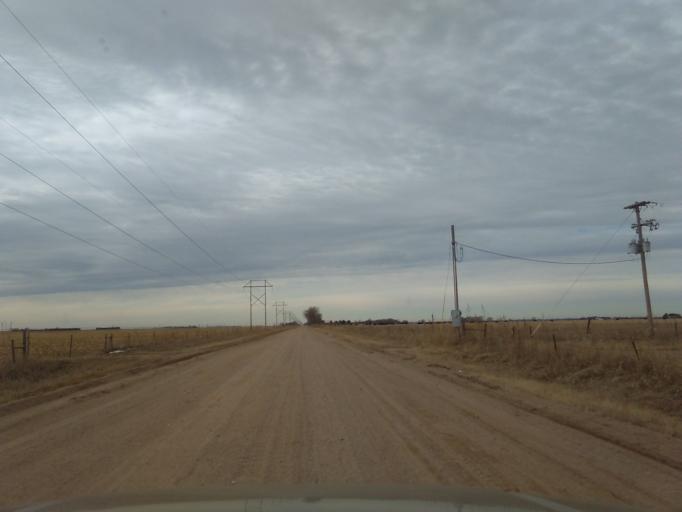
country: US
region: Nebraska
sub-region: Buffalo County
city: Shelton
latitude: 40.6548
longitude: -98.7477
